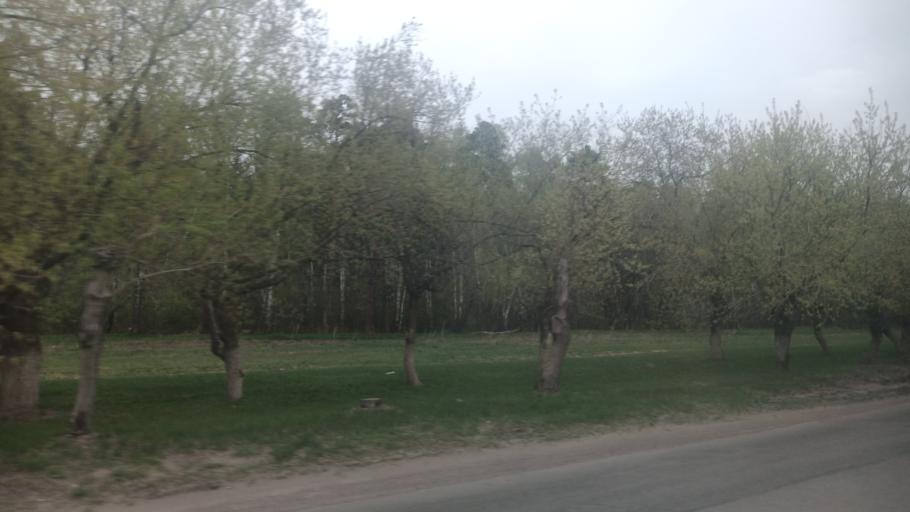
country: RU
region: Altai Krai
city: Yuzhnyy
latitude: 53.2562
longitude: 83.6867
